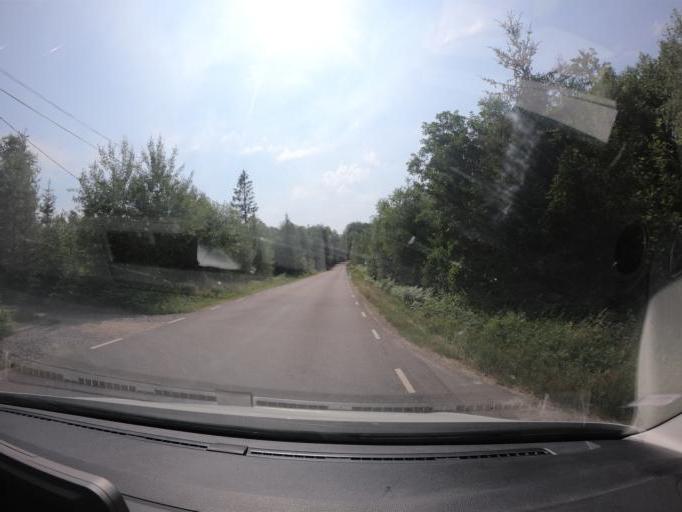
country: SE
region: Skane
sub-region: Hassleholms Kommun
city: Bjarnum
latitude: 56.3309
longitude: 13.6193
